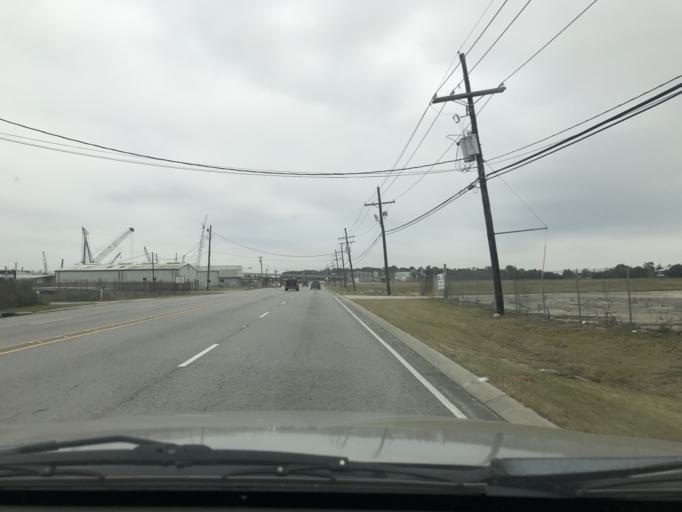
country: US
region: Louisiana
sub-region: Jefferson Parish
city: Woodmere
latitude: 29.8774
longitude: -90.0744
